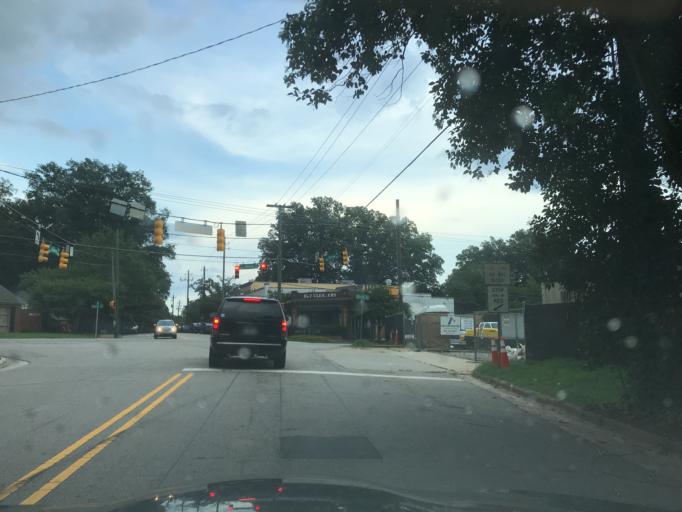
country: US
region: North Carolina
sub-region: Wake County
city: West Raleigh
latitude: 35.8094
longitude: -78.6561
